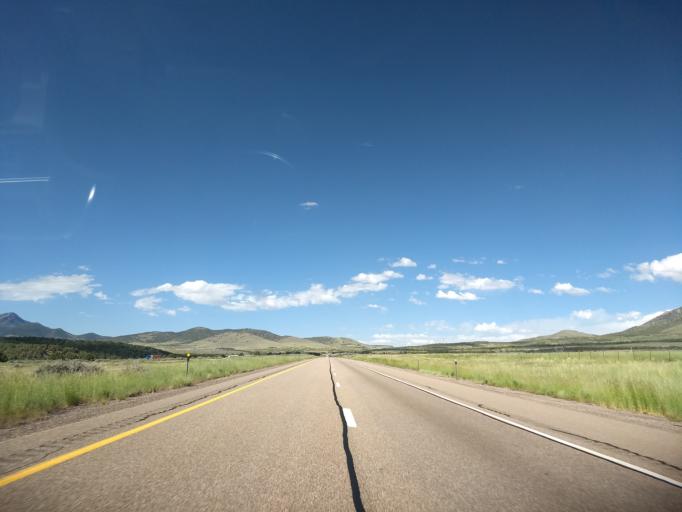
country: US
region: Utah
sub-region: Millard County
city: Fillmore
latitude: 39.1688
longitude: -112.2148
